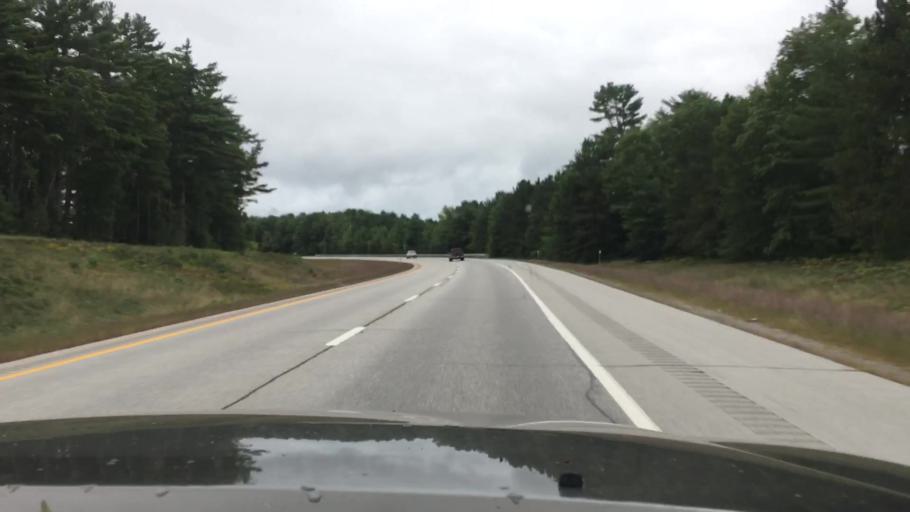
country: US
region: New Hampshire
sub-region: Belknap County
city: Sanbornton
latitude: 43.5104
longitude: -71.6178
